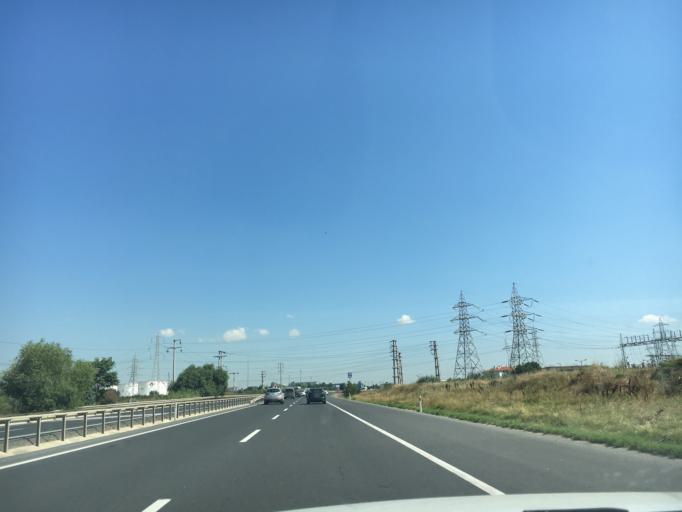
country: TR
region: Tekirdag
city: Marmara Ereglisi
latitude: 40.9924
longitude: 27.9727
